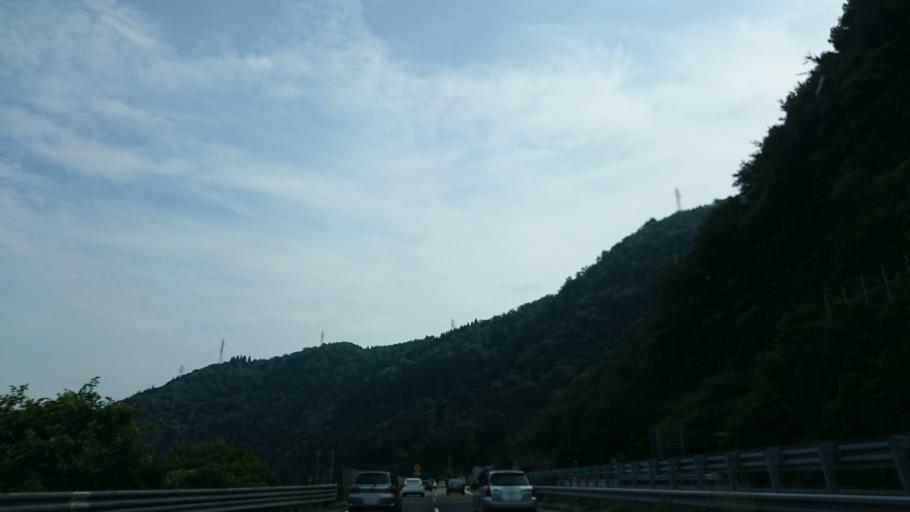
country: JP
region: Gifu
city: Gujo
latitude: 35.7429
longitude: 136.9447
